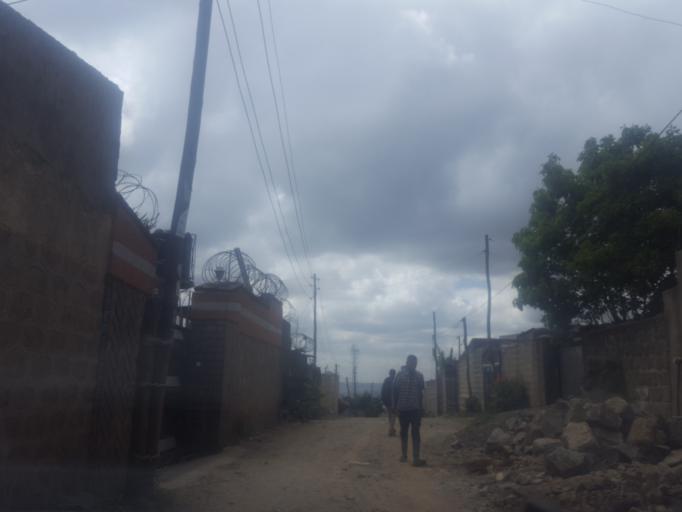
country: ET
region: Adis Abeba
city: Addis Ababa
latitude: 9.0643
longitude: 38.7351
